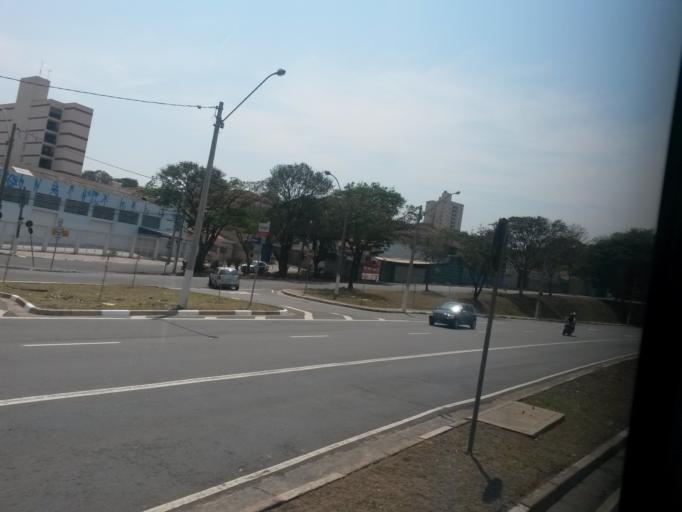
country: BR
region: Sao Paulo
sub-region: Campinas
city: Campinas
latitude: -22.8995
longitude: -47.0877
